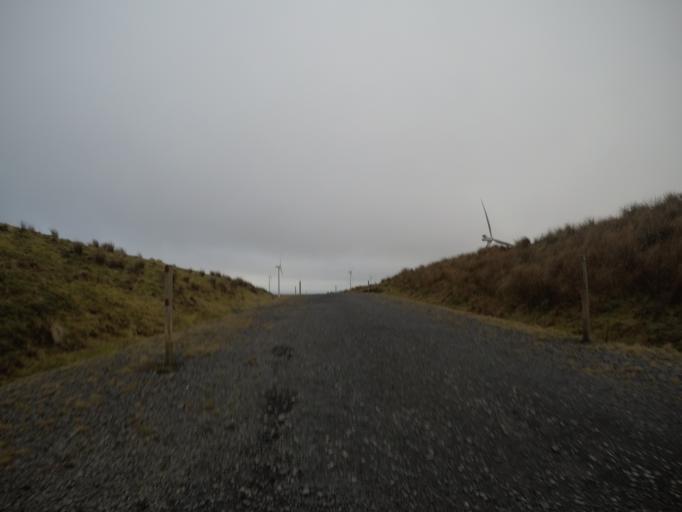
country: GB
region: Scotland
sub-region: North Ayrshire
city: Fairlie
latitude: 55.7431
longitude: -4.7918
